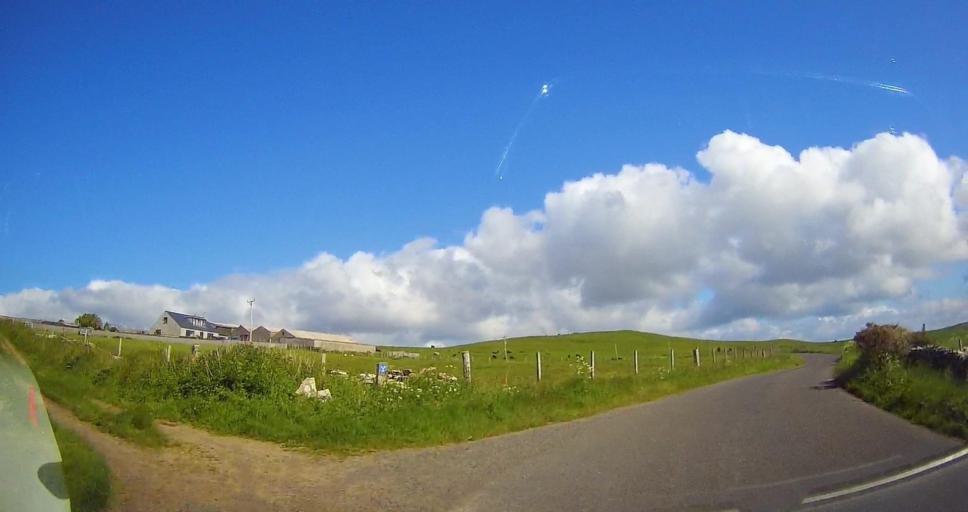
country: GB
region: Scotland
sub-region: Orkney Islands
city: Stromness
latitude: 58.9827
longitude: -3.1405
